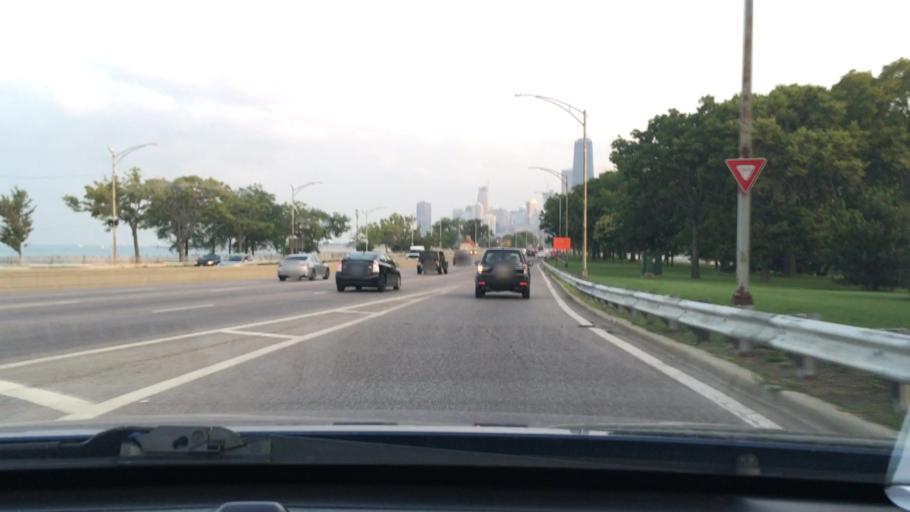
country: US
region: Illinois
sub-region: Cook County
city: Chicago
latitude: 41.9247
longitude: -87.6311
